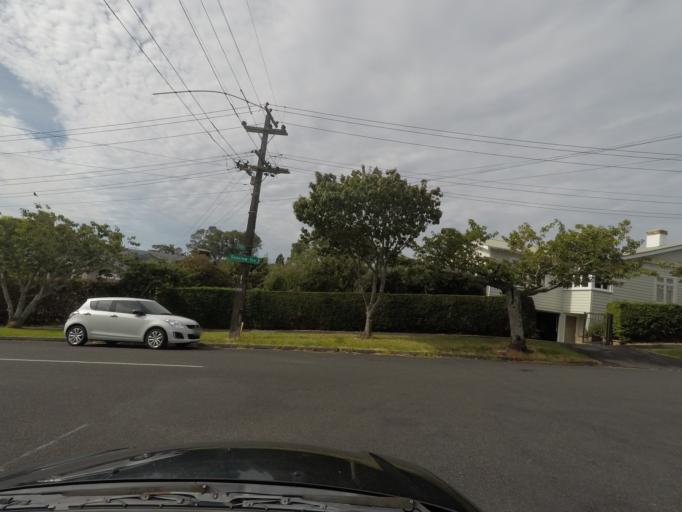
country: NZ
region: Auckland
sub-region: Auckland
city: Rosebank
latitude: -36.8800
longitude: 174.7149
